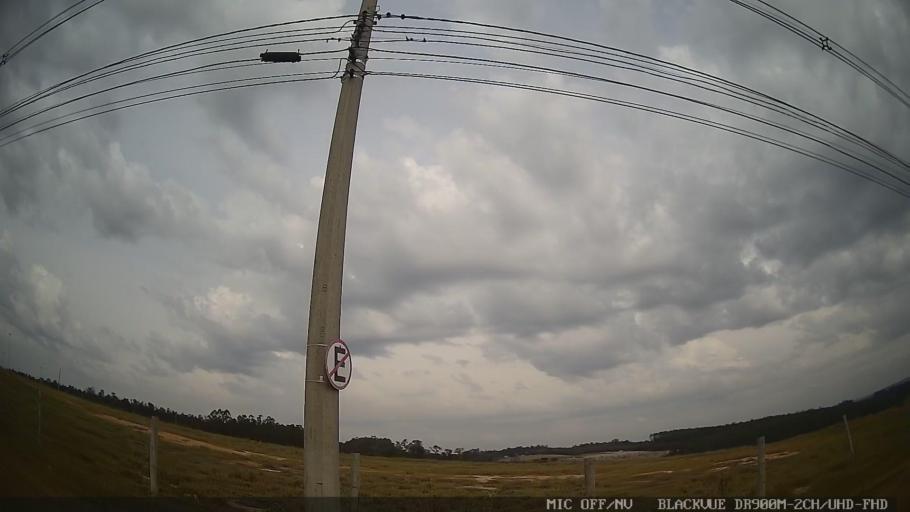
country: BR
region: Sao Paulo
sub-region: Indaiatuba
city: Indaiatuba
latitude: -23.1321
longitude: -47.2552
